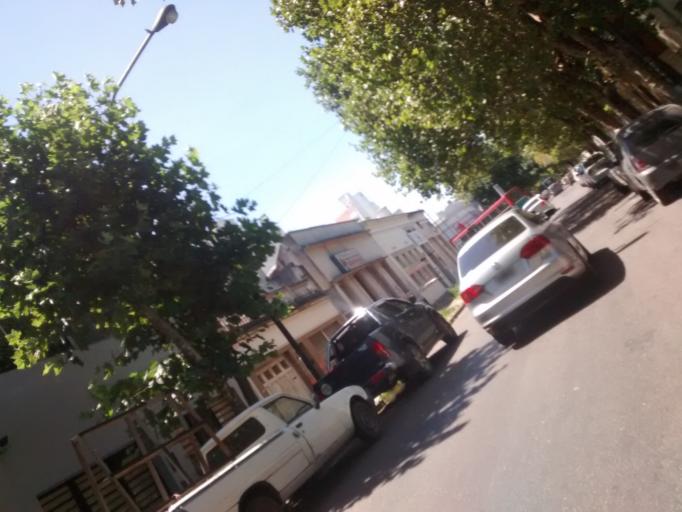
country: AR
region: Buenos Aires
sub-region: Partido de La Plata
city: La Plata
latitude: -34.9040
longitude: -57.9531
